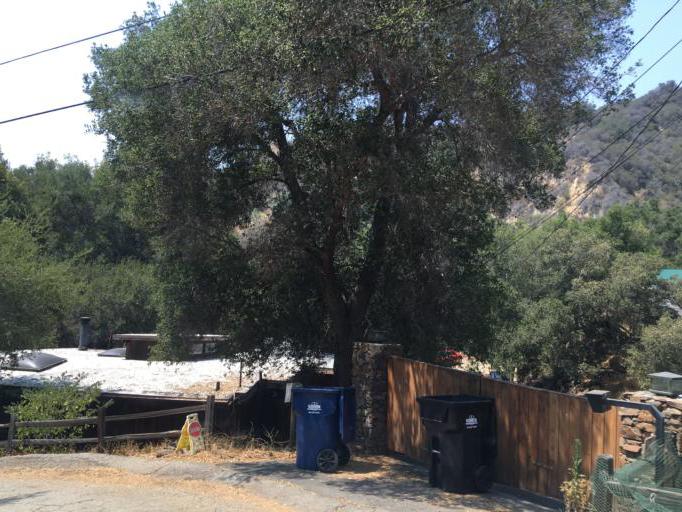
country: US
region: California
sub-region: Los Angeles County
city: Topanga
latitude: 34.0982
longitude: -118.5982
